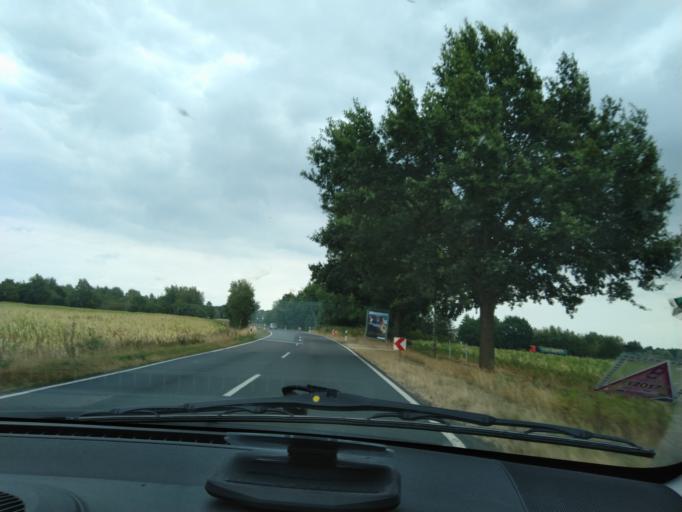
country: DE
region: Lower Saxony
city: Rhede
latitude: 53.0667
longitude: 7.2190
